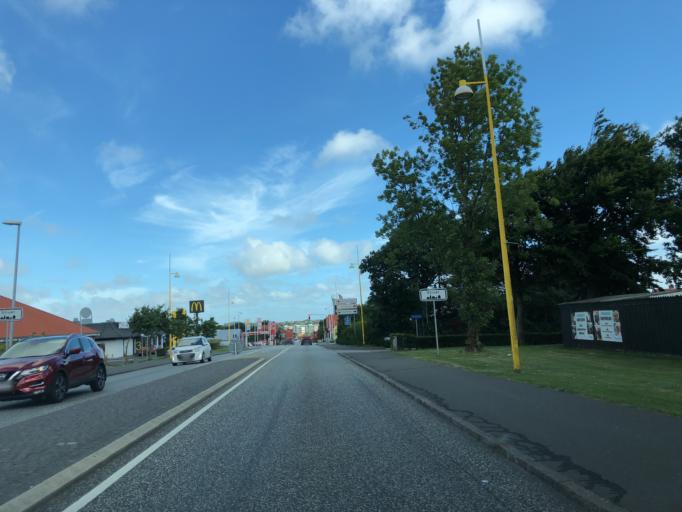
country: DK
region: Central Jutland
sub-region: Struer Kommune
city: Struer
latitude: 56.4867
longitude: 8.5837
